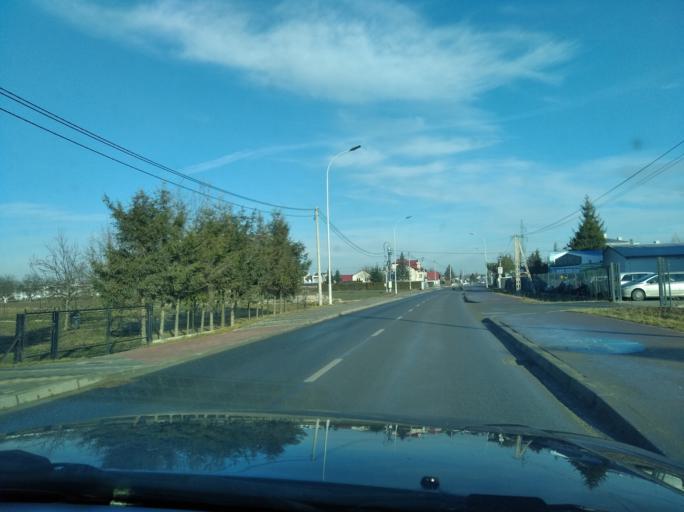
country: PL
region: Subcarpathian Voivodeship
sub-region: Powiat rzeszowski
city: Boguchwala
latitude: 49.9842
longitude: 21.9897
